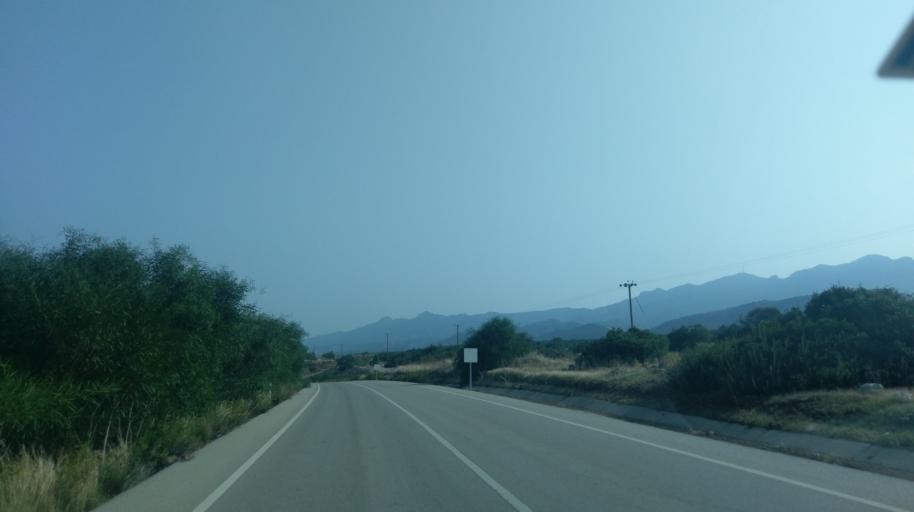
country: CY
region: Ammochostos
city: Trikomo
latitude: 35.4097
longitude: 33.8236
